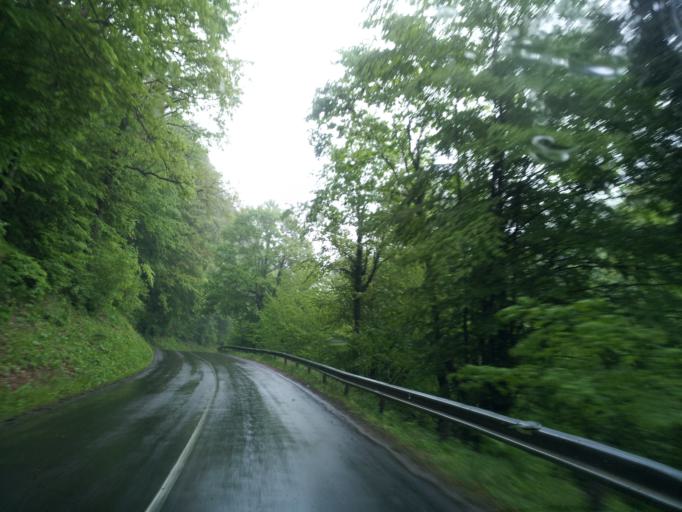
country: HU
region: Baranya
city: Komlo
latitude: 46.2164
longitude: 18.3011
